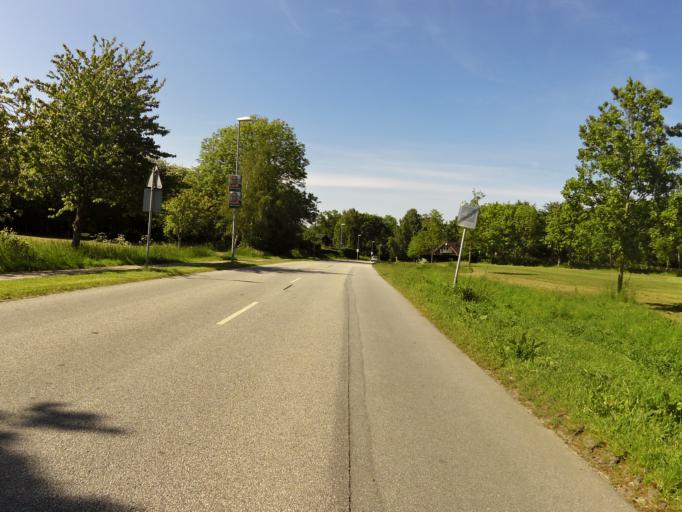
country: DK
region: South Denmark
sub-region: Haderslev Kommune
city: Gram
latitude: 55.2907
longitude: 9.0562
